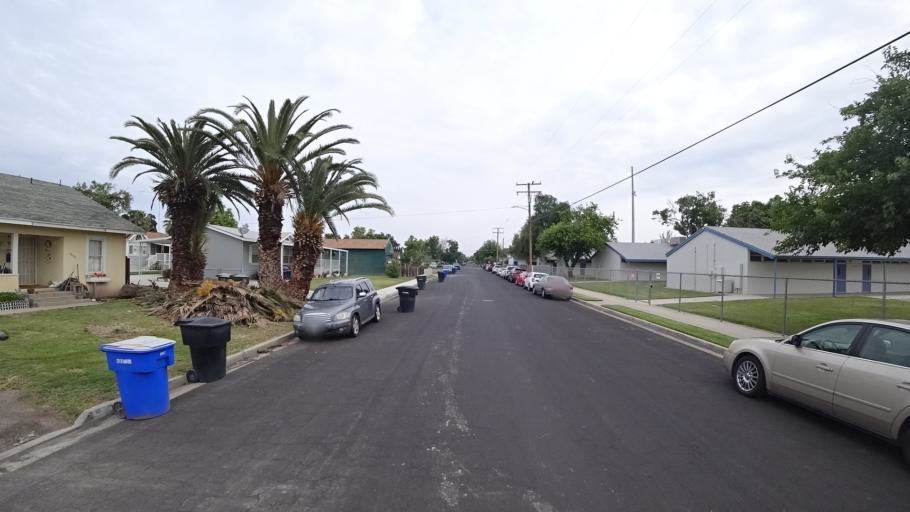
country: US
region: California
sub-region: Kings County
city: Hanford
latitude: 36.3377
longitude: -119.6537
